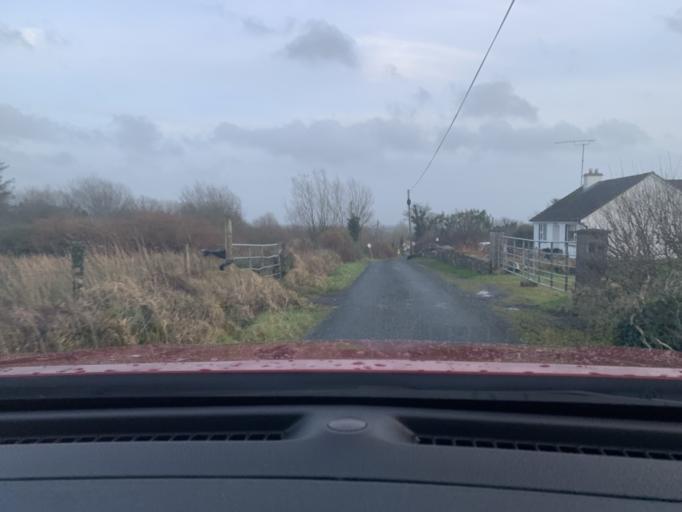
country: IE
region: Connaught
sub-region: Roscommon
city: Ballaghaderreen
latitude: 53.9444
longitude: -8.5002
